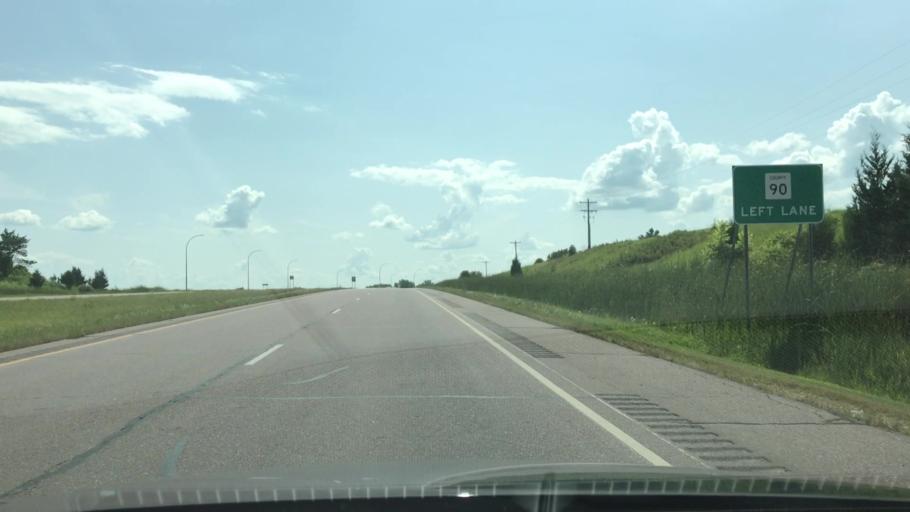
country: US
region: Minnesota
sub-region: Nicollet County
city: North Mankato
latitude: 44.1478
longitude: -94.0803
